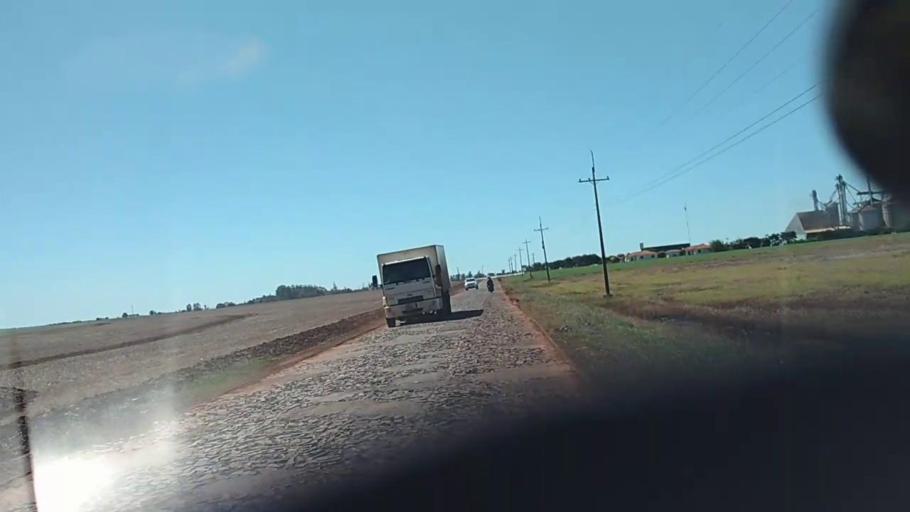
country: PY
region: Alto Parana
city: Naranjal
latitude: -25.9730
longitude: -55.1541
